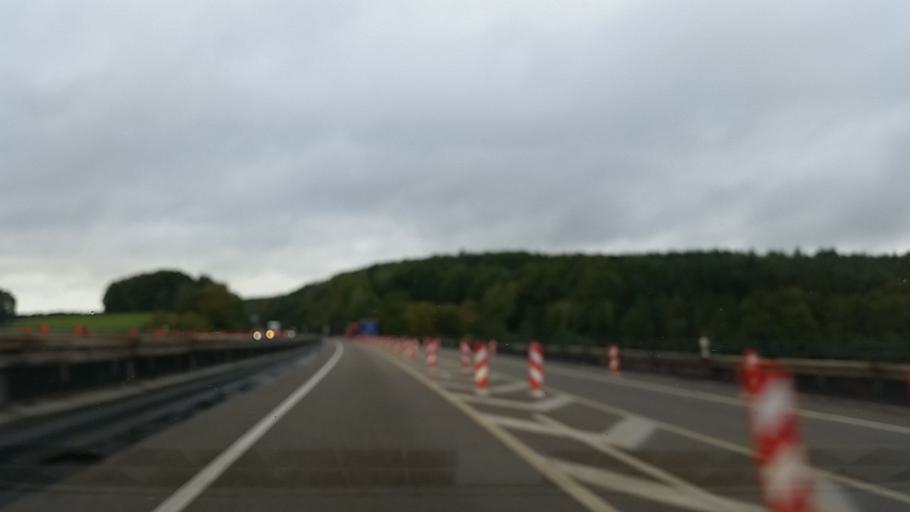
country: DE
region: Bavaria
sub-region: Regierungsbezirk Unterfranken
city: Motten
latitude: 50.4423
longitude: 9.7429
